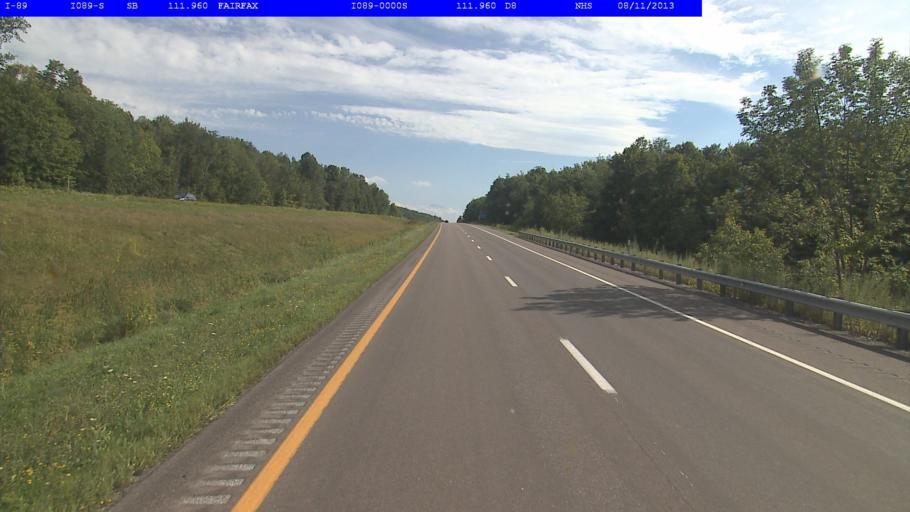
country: US
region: Vermont
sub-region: Franklin County
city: Saint Albans
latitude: 44.7696
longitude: -73.0759
